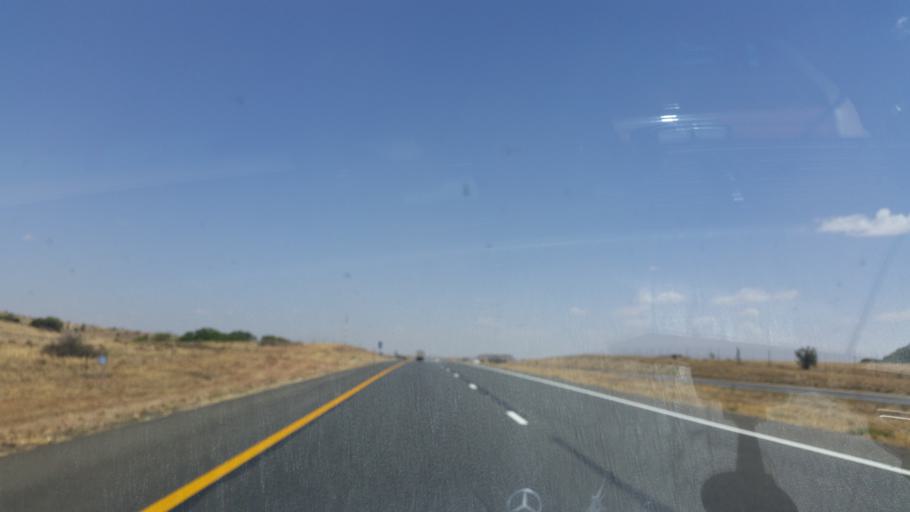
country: ZA
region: Orange Free State
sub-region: Lejweleputswa District Municipality
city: Brandfort
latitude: -28.9280
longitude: 26.4300
